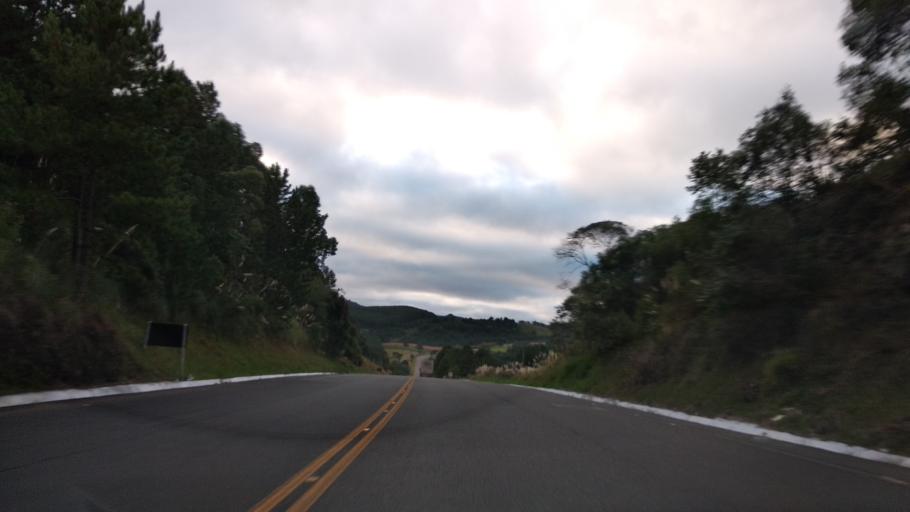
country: BR
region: Santa Catarina
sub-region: Campos Novos
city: Campos Novos
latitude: -27.4952
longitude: -50.9650
